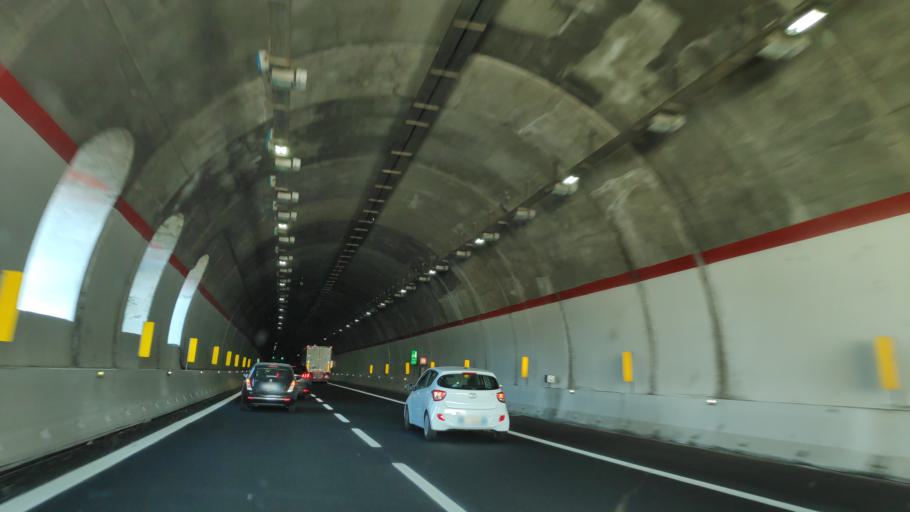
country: IT
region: Basilicate
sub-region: Provincia di Potenza
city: Lagonegro
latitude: 40.1396
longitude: 15.7580
